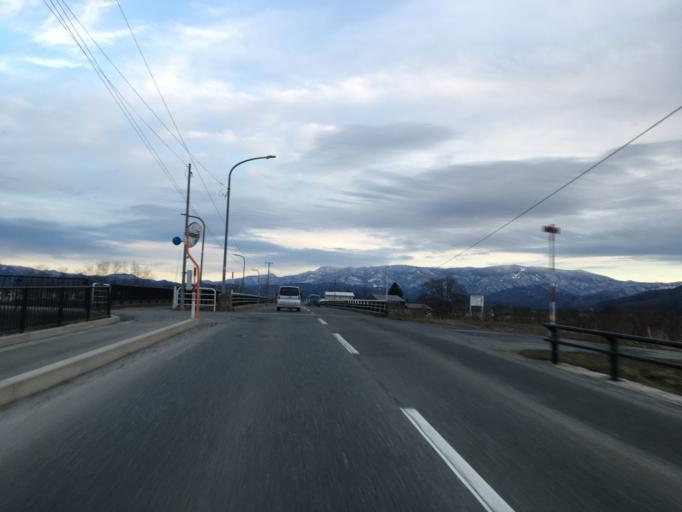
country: JP
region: Yamagata
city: Yonezawa
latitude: 37.9286
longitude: 140.0818
